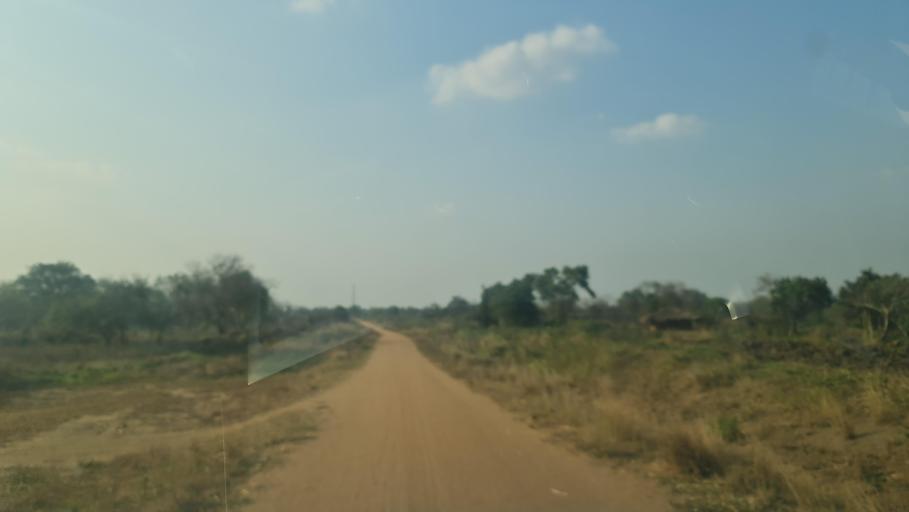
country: MZ
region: Zambezia
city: Quelimane
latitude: -18.1552
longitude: 35.9906
